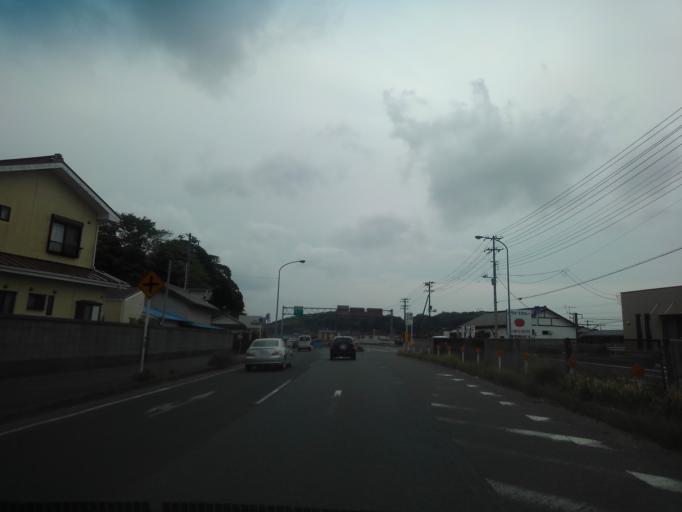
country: JP
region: Chiba
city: Kisarazu
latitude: 35.3650
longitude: 139.9235
